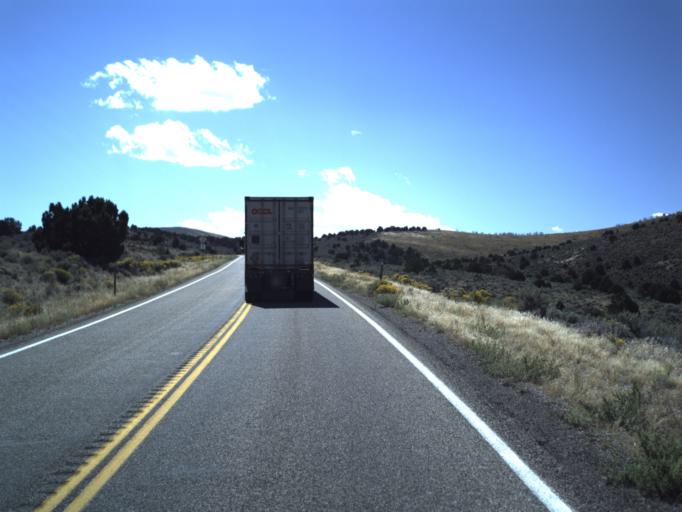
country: US
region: Utah
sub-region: Beaver County
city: Milford
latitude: 38.1173
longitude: -112.9520
